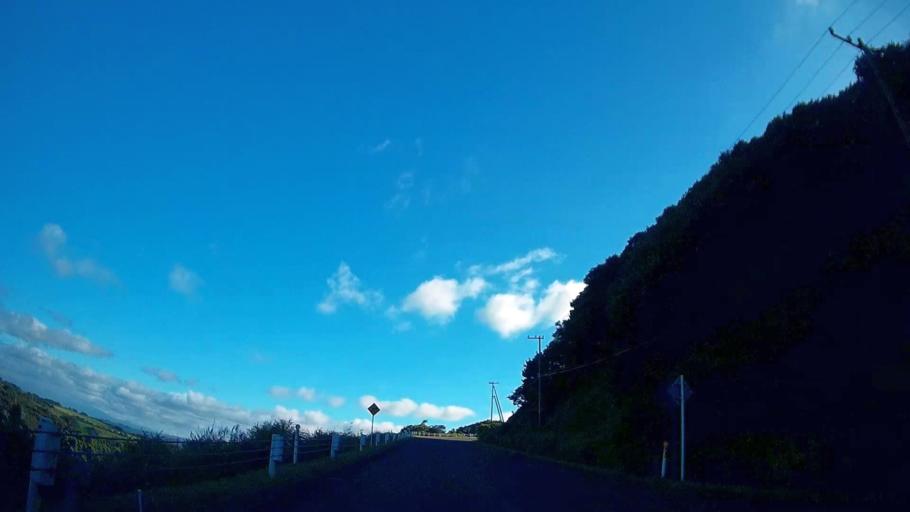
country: JP
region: Hokkaido
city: Iwanai
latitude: 42.4588
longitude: 139.8578
